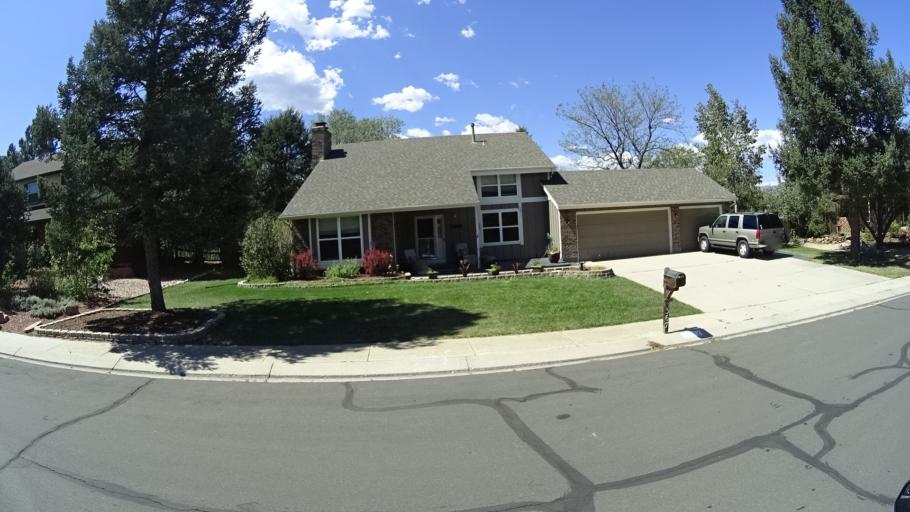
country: US
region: Colorado
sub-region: El Paso County
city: Colorado Springs
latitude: 38.7882
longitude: -104.8350
